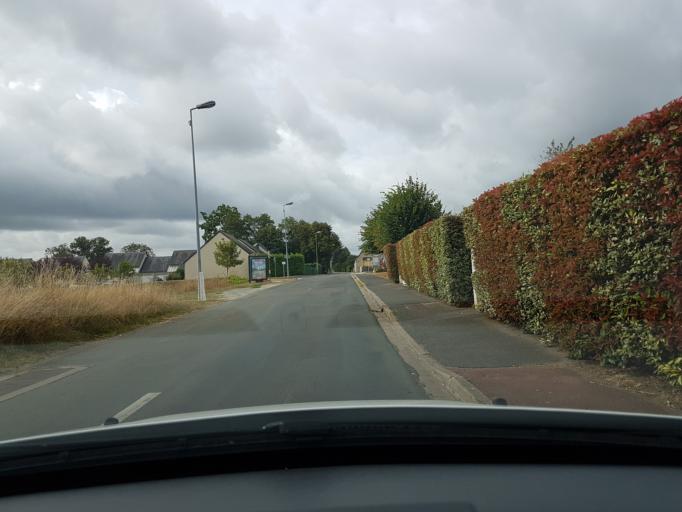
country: FR
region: Centre
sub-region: Departement d'Indre-et-Loire
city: Larcay
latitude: 47.3647
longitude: 0.7770
